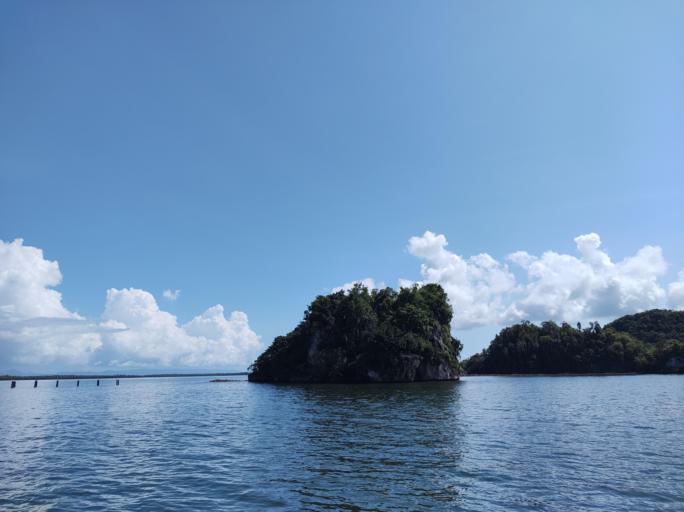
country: DO
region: Hato Mayor
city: Sabana de La Mar
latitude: 19.0812
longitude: -69.4709
